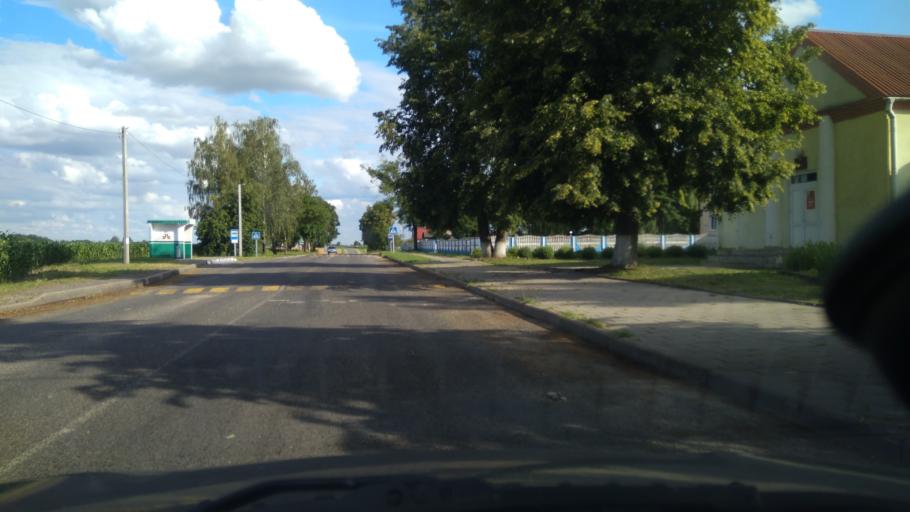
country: BY
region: Grodnenskaya
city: Masty
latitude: 53.3208
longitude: 24.6861
